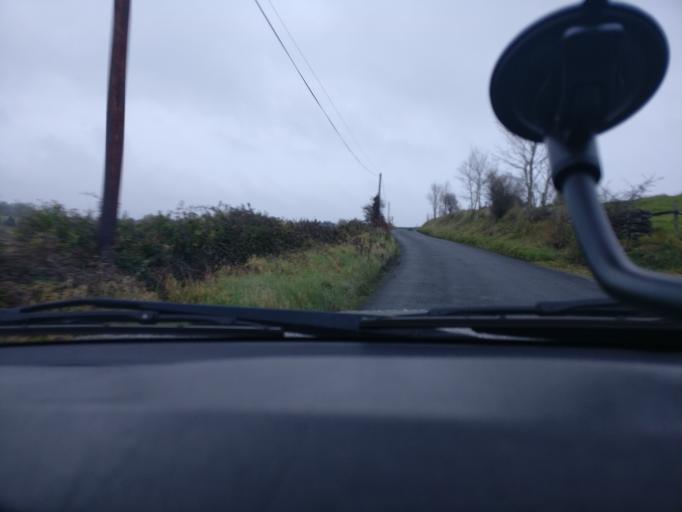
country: IE
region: Connaught
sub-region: County Galway
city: Loughrea
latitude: 53.2088
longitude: -8.5515
